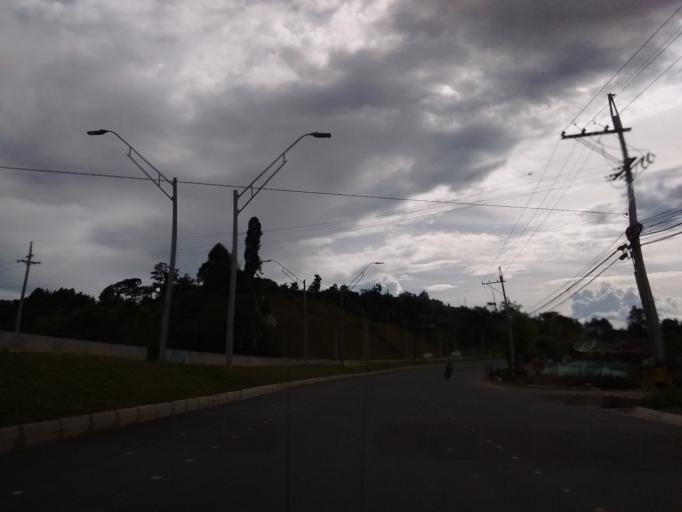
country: CO
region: Antioquia
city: Santuario
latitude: 6.1340
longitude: -75.2890
